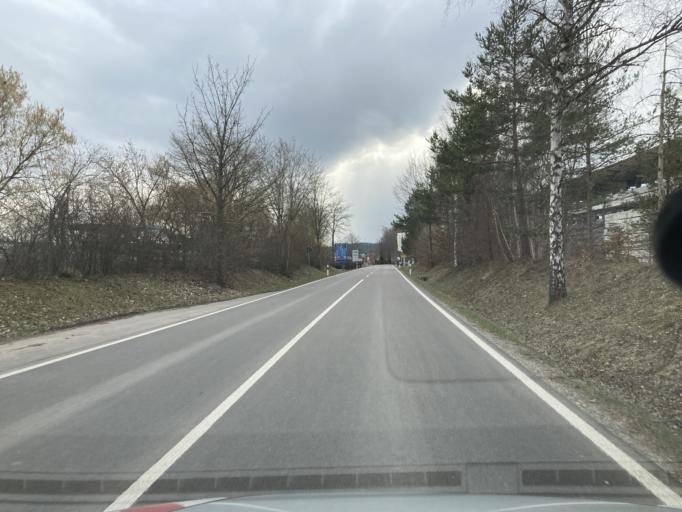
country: DE
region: Baden-Wuerttemberg
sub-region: Karlsruhe Region
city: Neuweiler
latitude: 48.6661
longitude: 8.6045
